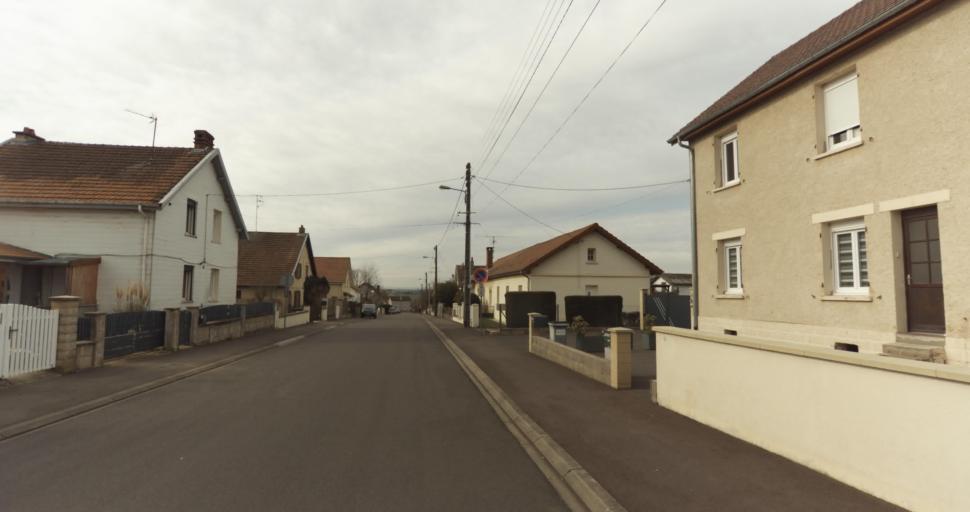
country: FR
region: Lorraine
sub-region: Departement de Meurthe-et-Moselle
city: Jarny
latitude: 49.1499
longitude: 5.8823
